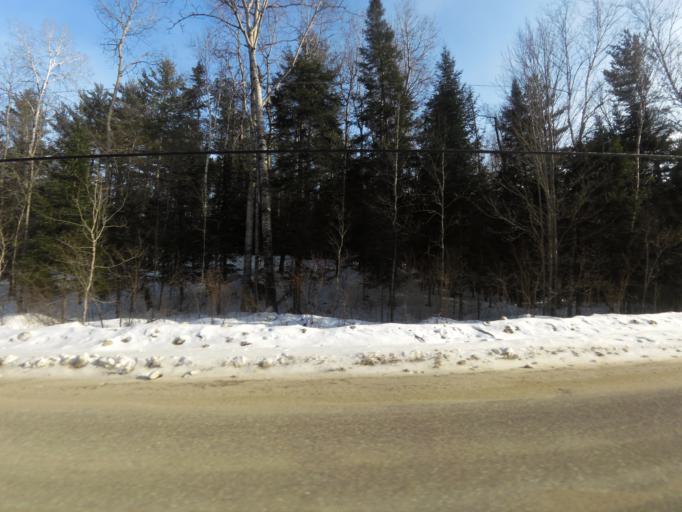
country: CA
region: Quebec
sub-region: Outaouais
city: Maniwaki
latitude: 46.2700
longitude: -75.8865
